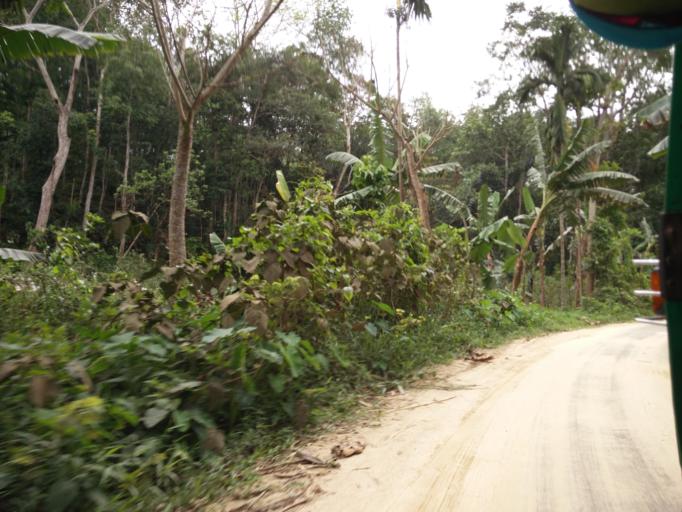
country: IN
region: Tripura
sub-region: Dhalai
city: Kamalpur
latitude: 24.3033
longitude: 91.7872
